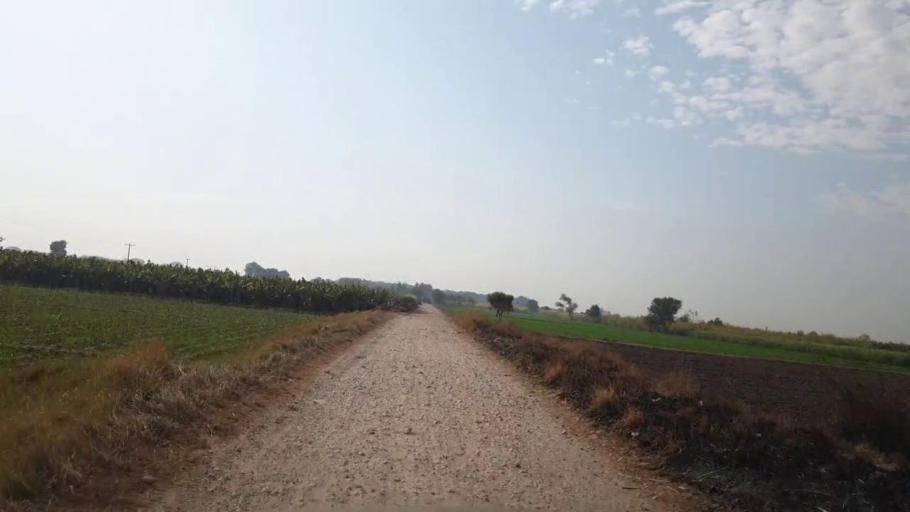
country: PK
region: Sindh
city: Matiari
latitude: 25.5624
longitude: 68.5200
